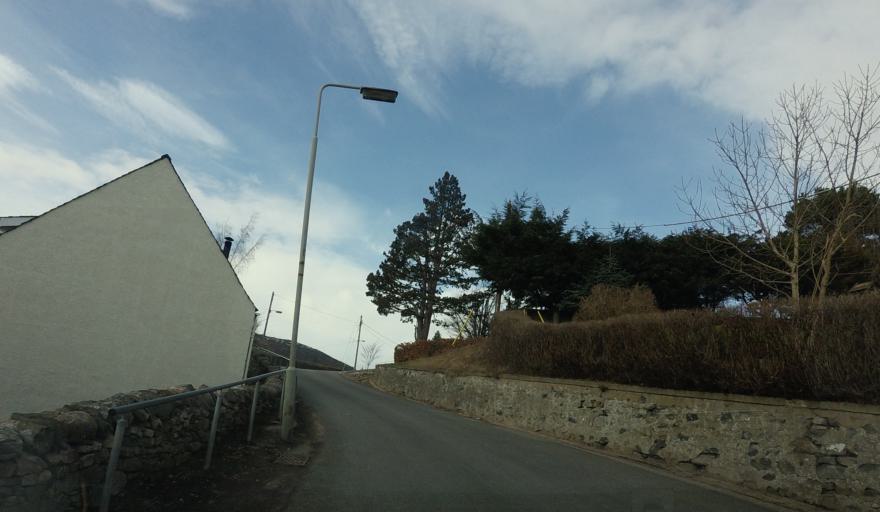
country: GB
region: Scotland
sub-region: Highland
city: Kingussie
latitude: 57.0807
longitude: -4.0515
